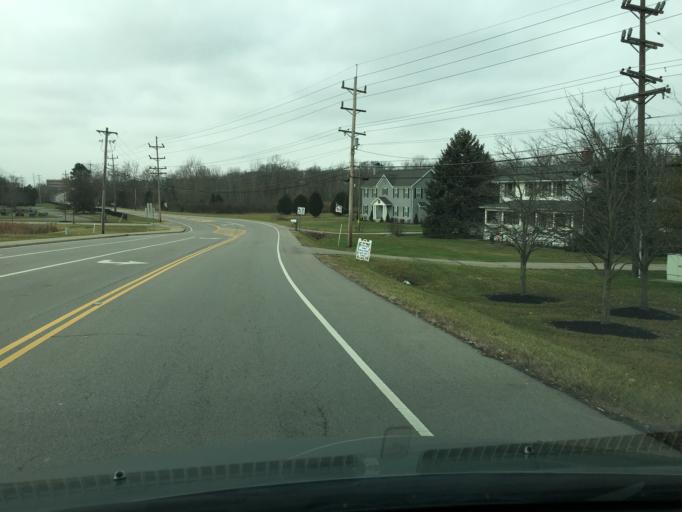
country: US
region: Ohio
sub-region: Butler County
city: Beckett Ridge
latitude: 39.3254
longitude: -84.4109
